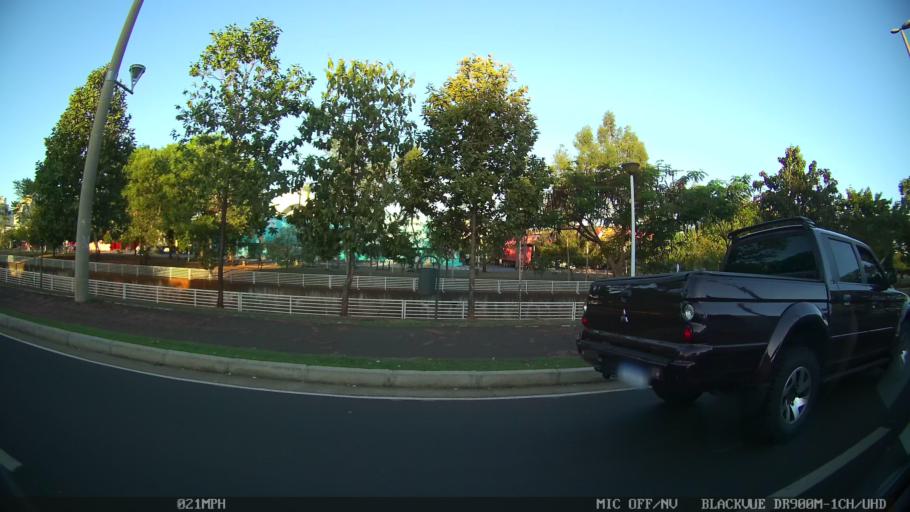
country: BR
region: Sao Paulo
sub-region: Sao Jose Do Rio Preto
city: Sao Jose do Rio Preto
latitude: -20.7978
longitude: -49.3773
